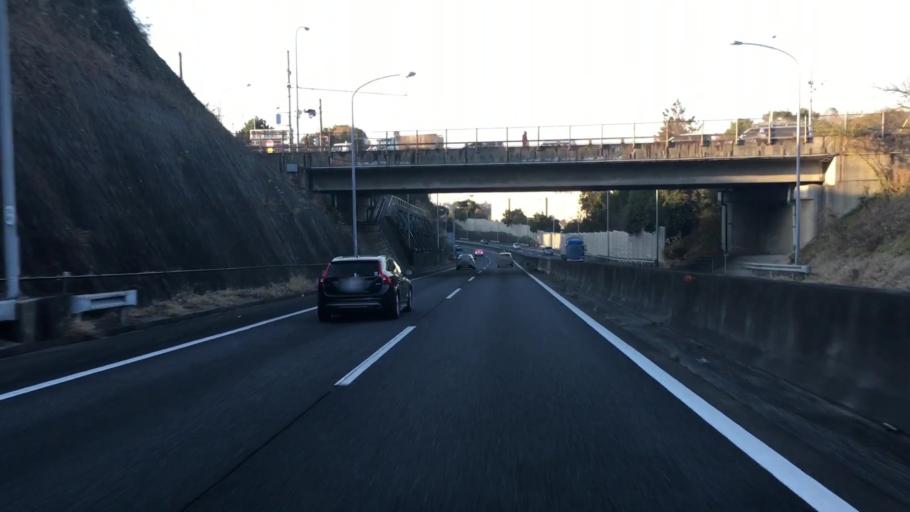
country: JP
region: Kanagawa
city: Kamakura
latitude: 35.3694
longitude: 139.5947
